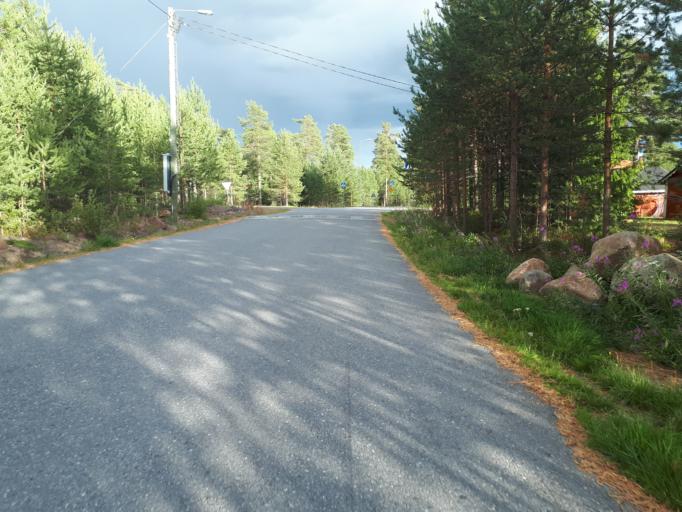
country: FI
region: Northern Ostrobothnia
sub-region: Oulunkaari
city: Ii
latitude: 65.3247
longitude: 25.4081
